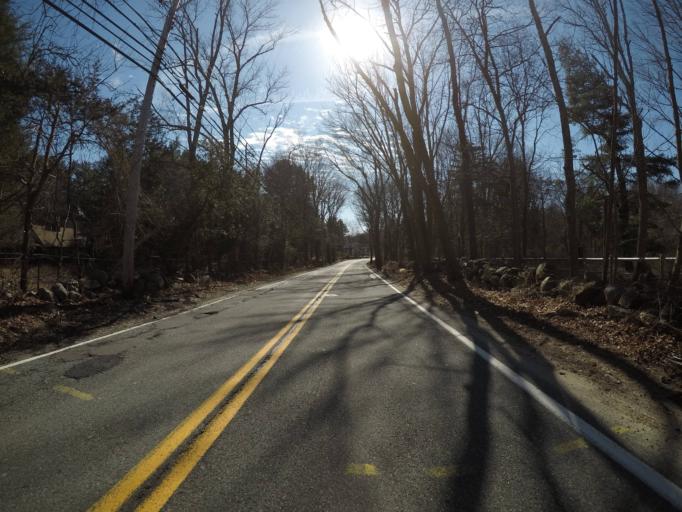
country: US
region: Massachusetts
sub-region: Norfolk County
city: Stoughton
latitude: 42.1028
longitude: -71.1314
